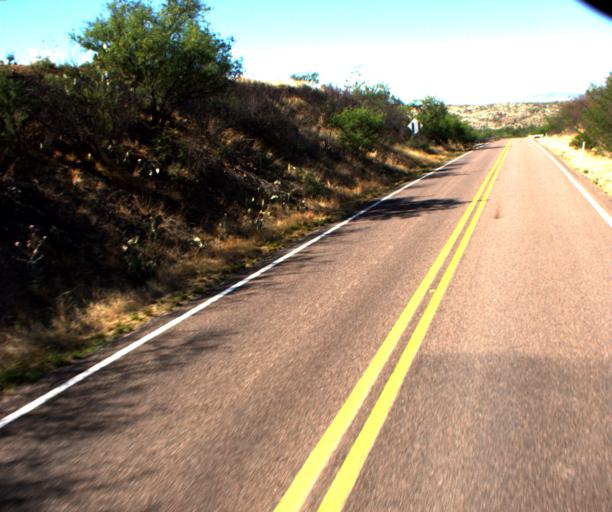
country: US
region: Arizona
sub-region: Pima County
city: Corona de Tucson
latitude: 31.8789
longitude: -110.6748
